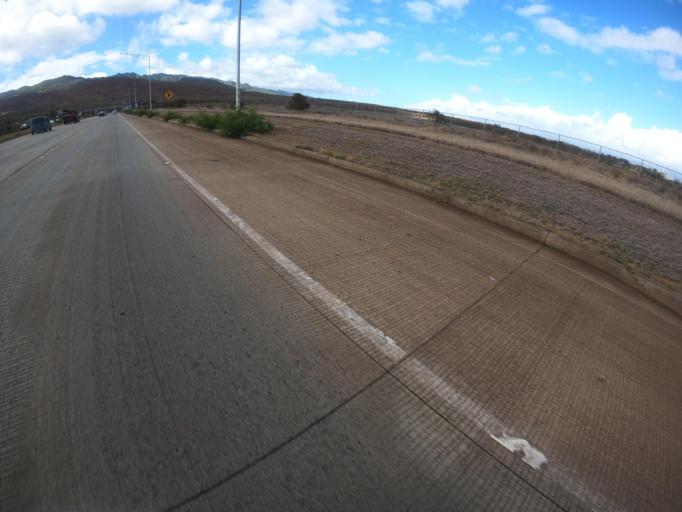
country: US
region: Hawaii
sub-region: Honolulu County
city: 'Ewa Villages
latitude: 21.3633
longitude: -158.0565
